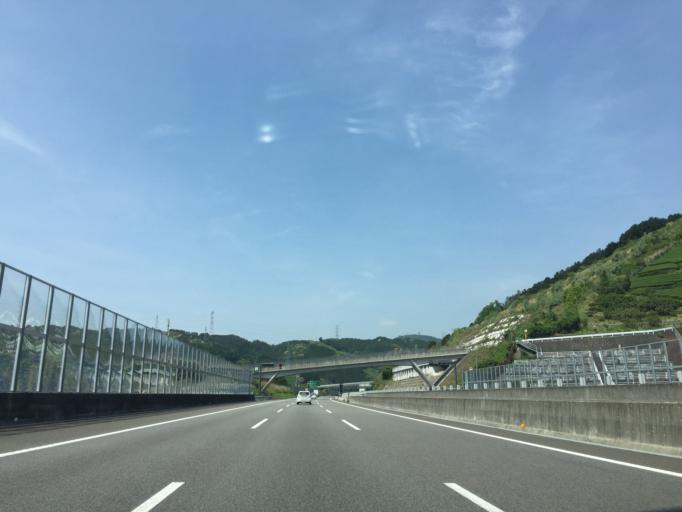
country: JP
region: Shizuoka
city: Kanaya
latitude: 34.8472
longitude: 138.1145
